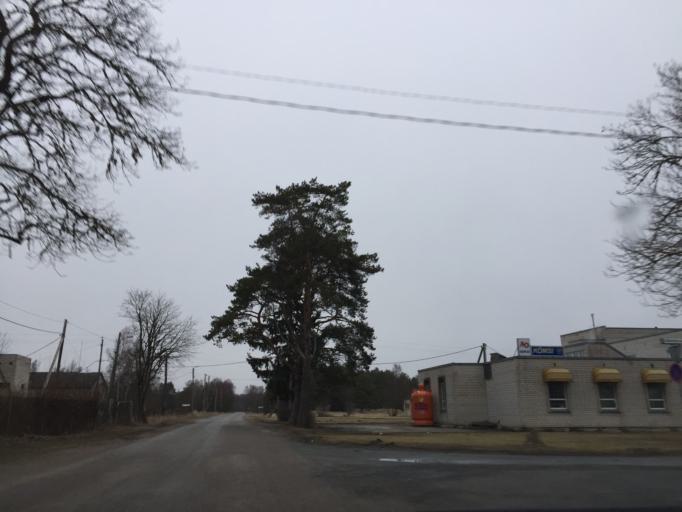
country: EE
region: Laeaene
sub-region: Lihula vald
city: Lihula
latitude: 58.6229
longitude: 23.6319
